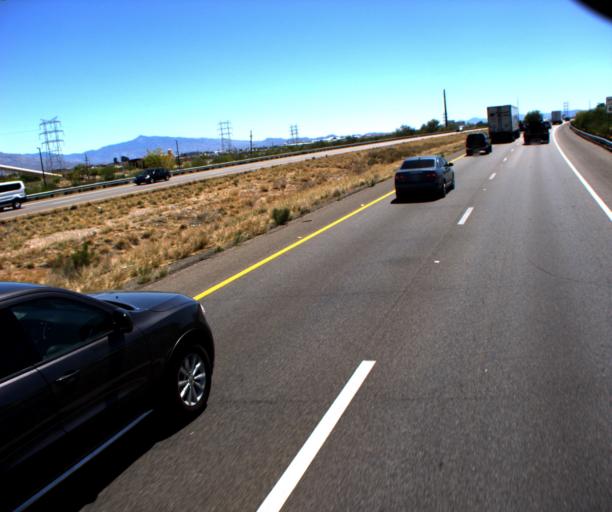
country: US
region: Arizona
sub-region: Pima County
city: Tucson
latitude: 32.1516
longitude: -110.8995
